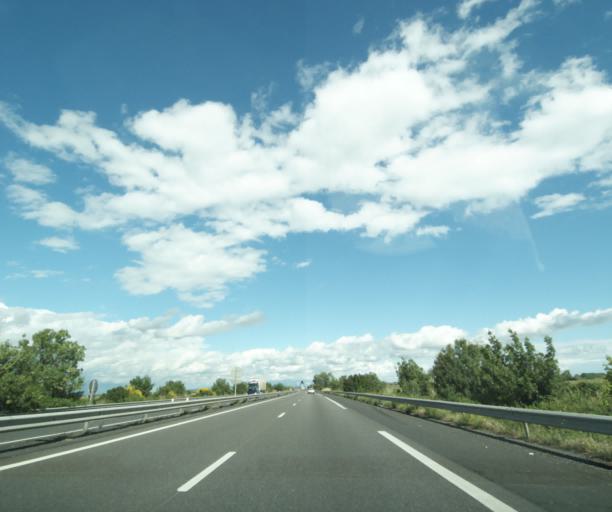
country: FR
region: Languedoc-Roussillon
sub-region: Departement du Gard
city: Bellegarde
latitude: 43.7305
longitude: 4.4859
